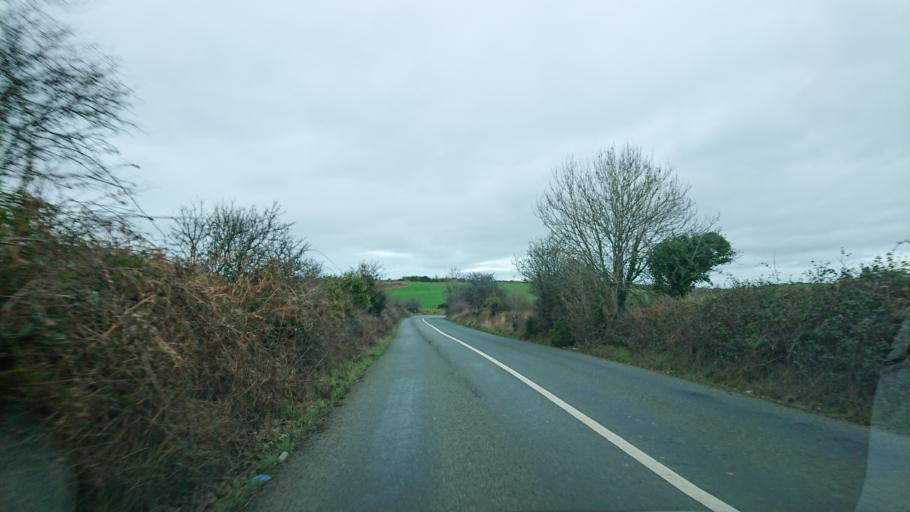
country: IE
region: Leinster
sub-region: Kilkenny
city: Mooncoin
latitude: 52.2123
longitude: -7.2444
